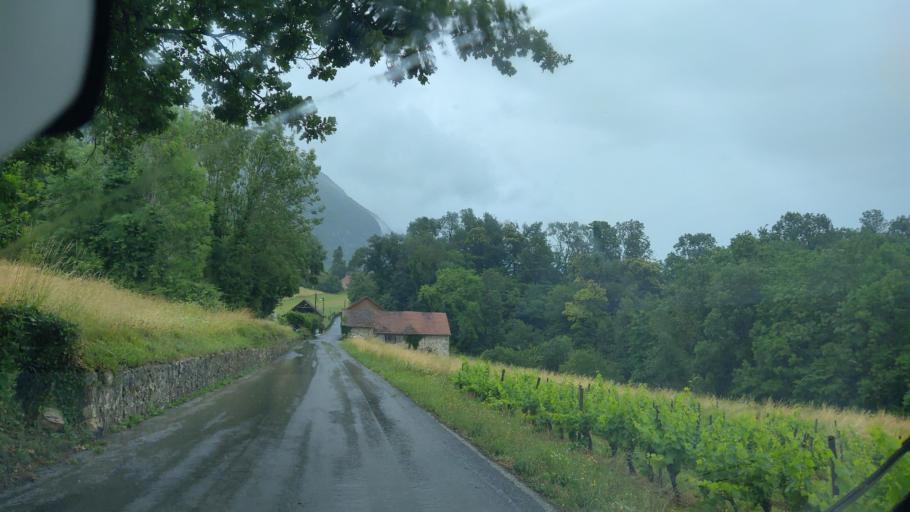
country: FR
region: Rhone-Alpes
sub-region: Departement de la Savoie
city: Chindrieux
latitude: 45.8294
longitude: 5.8487
